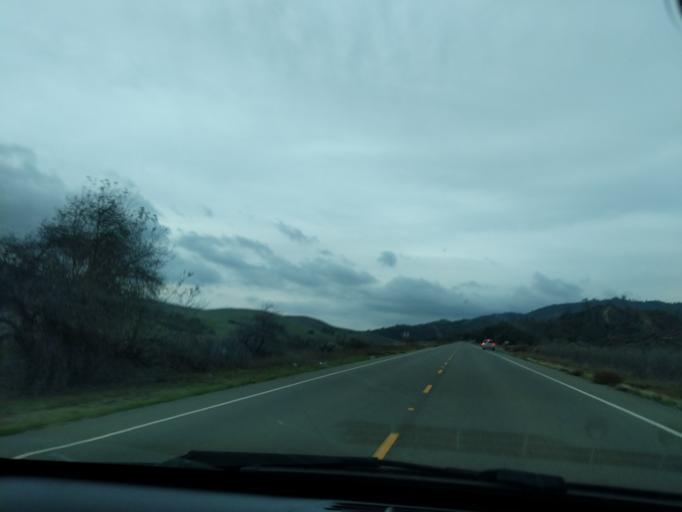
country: US
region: California
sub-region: Monterey County
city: Soledad
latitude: 36.6274
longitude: -121.2242
